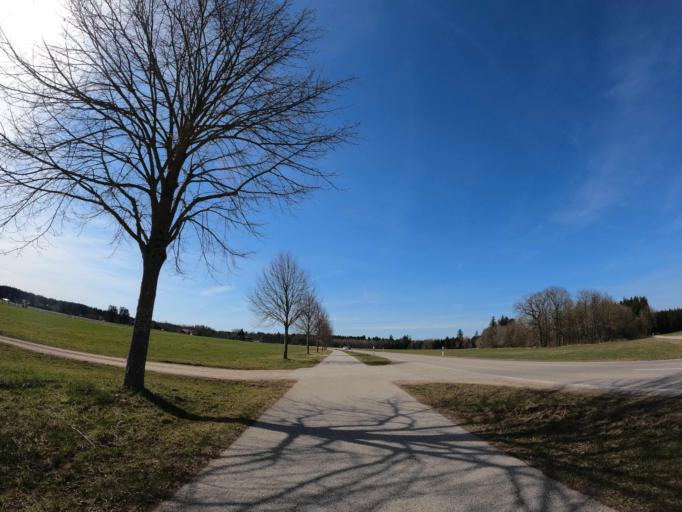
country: DE
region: Bavaria
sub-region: Upper Bavaria
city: Sauerlach
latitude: 47.9967
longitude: 11.6499
